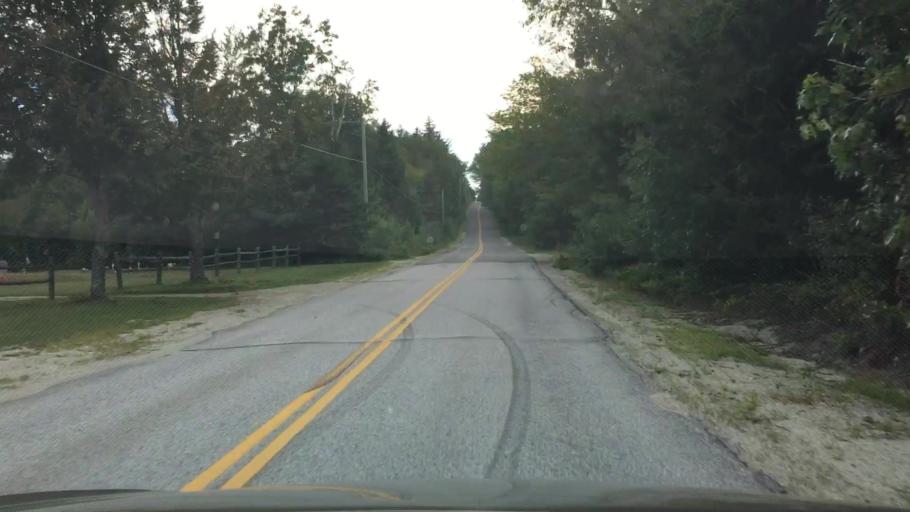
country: US
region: Maine
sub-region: Hancock County
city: Penobscot
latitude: 44.4449
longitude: -68.6280
